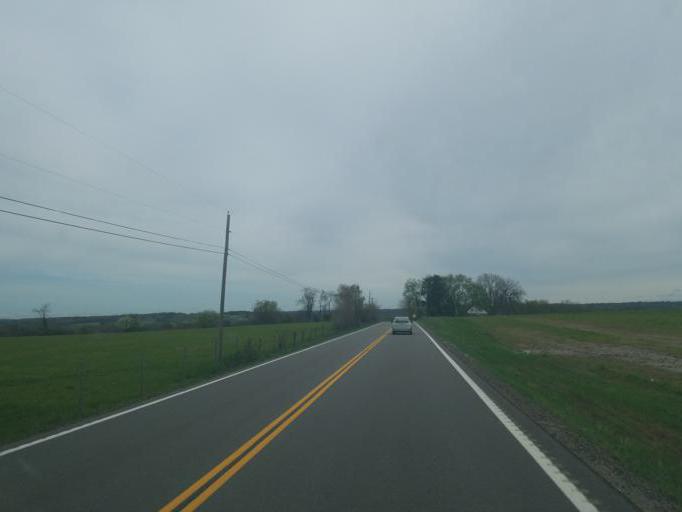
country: US
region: Ohio
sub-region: Wayne County
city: Rittman
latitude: 40.9366
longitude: -81.7502
